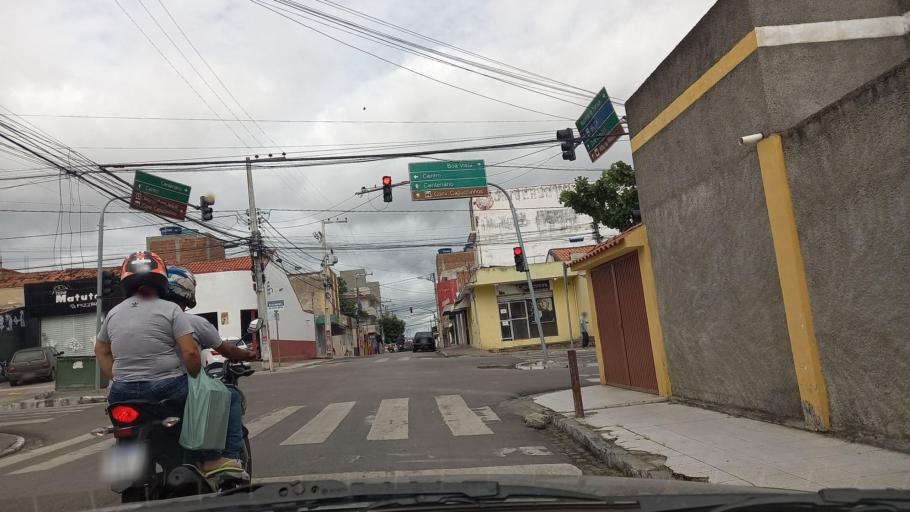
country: BR
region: Pernambuco
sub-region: Caruaru
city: Caruaru
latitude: -8.2793
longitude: -35.9768
